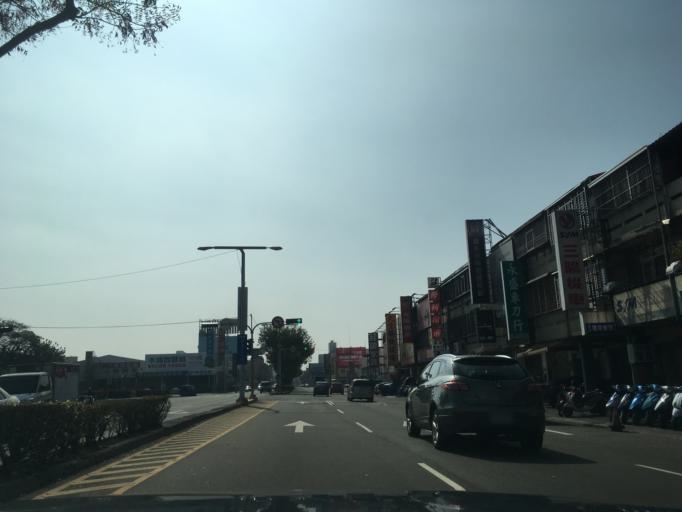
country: TW
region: Taiwan
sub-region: Taichung City
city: Taichung
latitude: 24.1993
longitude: 120.6560
